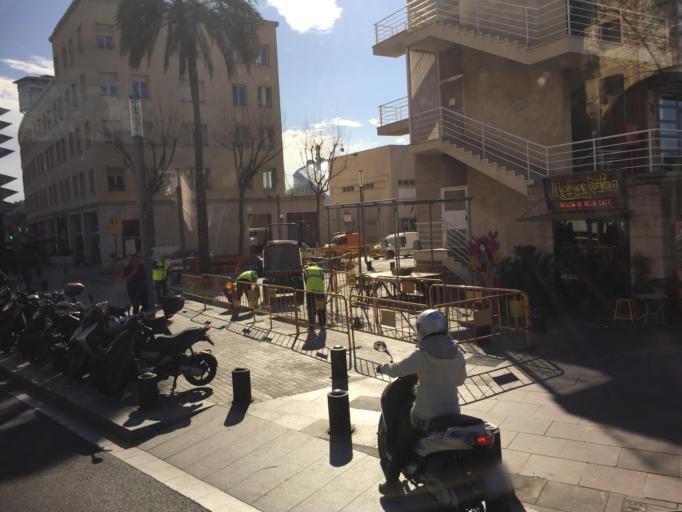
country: ES
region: Catalonia
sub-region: Provincia de Barcelona
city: Ciutat Vella
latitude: 41.3758
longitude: 2.1888
